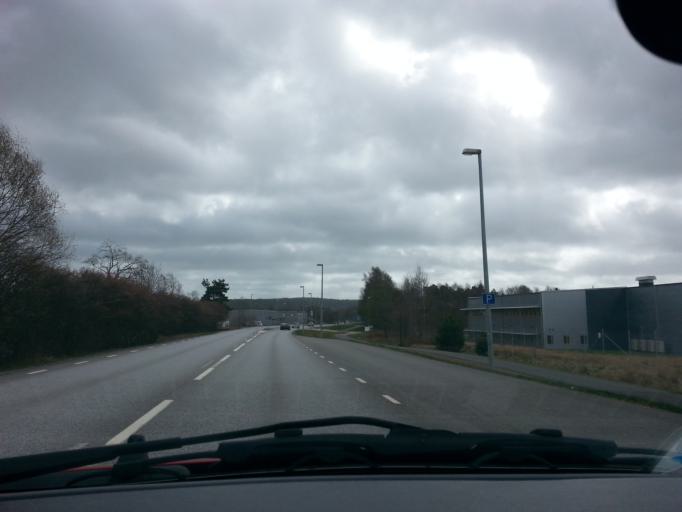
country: SE
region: Vaestra Goetaland
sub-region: Lerums Kommun
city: Stenkullen
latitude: 57.8003
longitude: 12.3074
